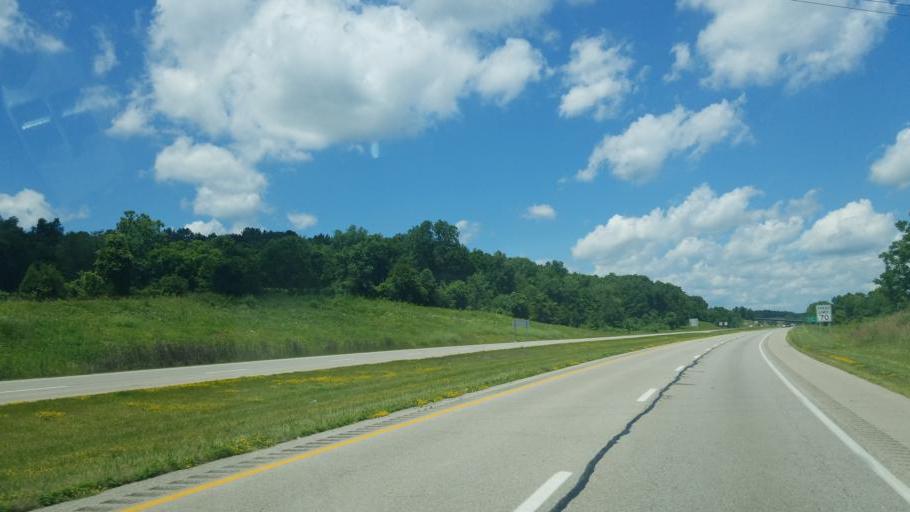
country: US
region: Ohio
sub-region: Gallia County
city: Gallipolis
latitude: 38.8522
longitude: -82.2433
